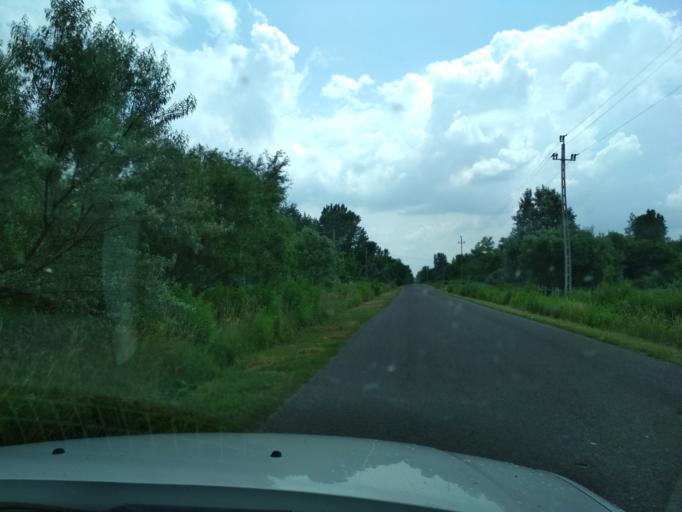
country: HU
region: Pest
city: Nagykata
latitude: 47.3948
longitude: 19.7583
